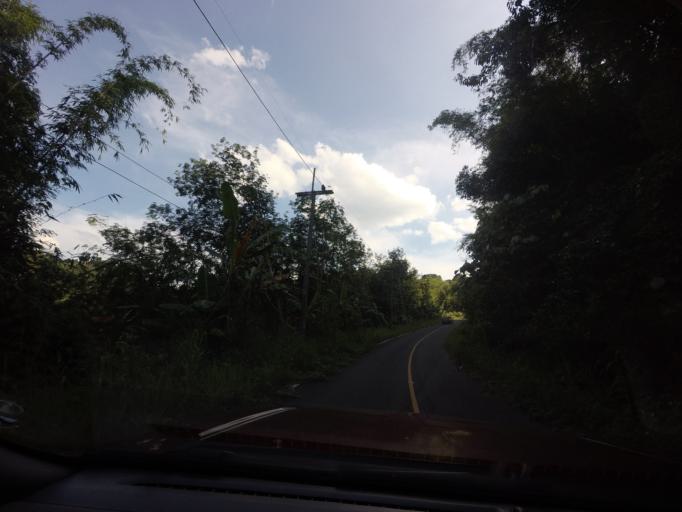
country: TH
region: Narathiwat
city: Si Sakhon
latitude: 6.0618
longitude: 101.3776
